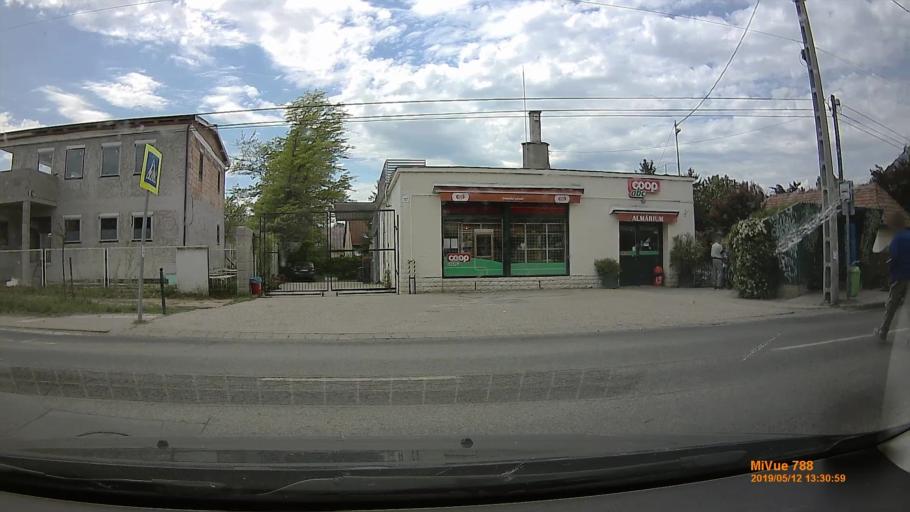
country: HU
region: Budapest
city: Budapest XVII. keruelet
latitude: 47.4774
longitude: 19.2927
